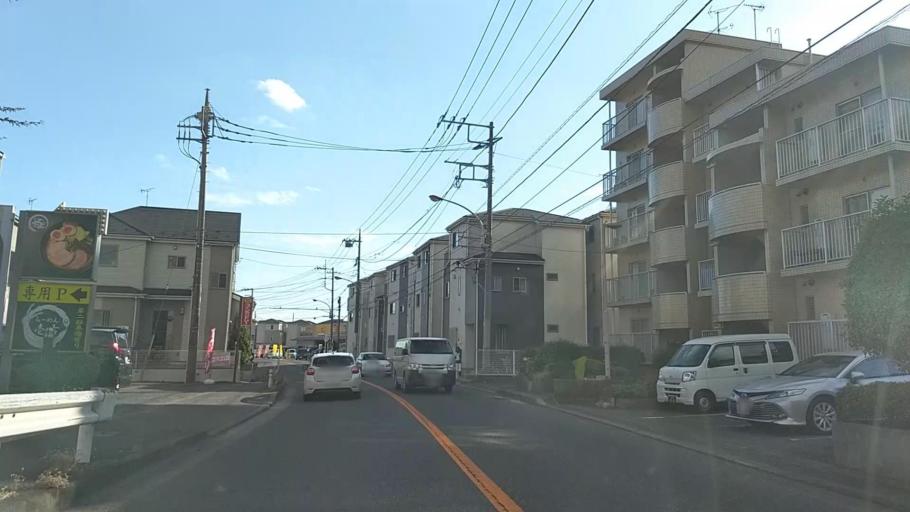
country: JP
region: Tokyo
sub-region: Machida-shi
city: Machida
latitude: 35.5836
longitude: 139.4971
